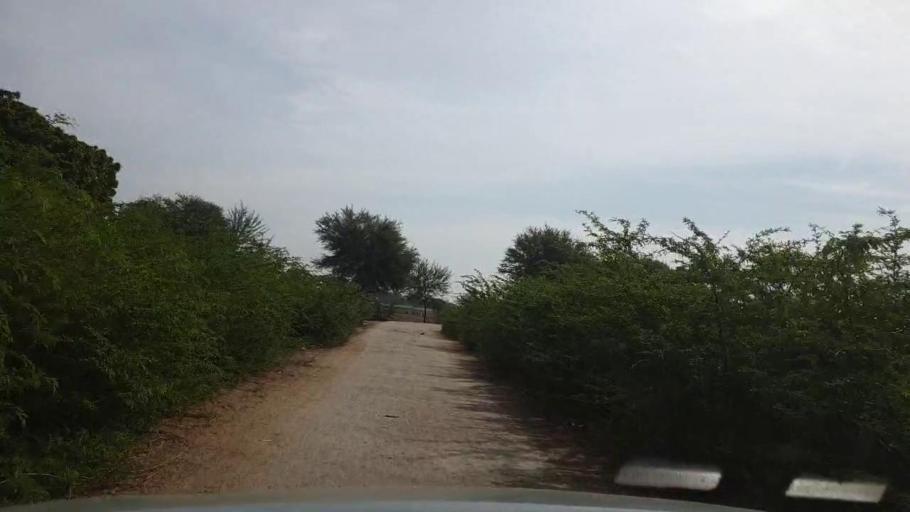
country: PK
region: Sindh
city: Kunri
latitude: 25.1509
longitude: 69.6038
